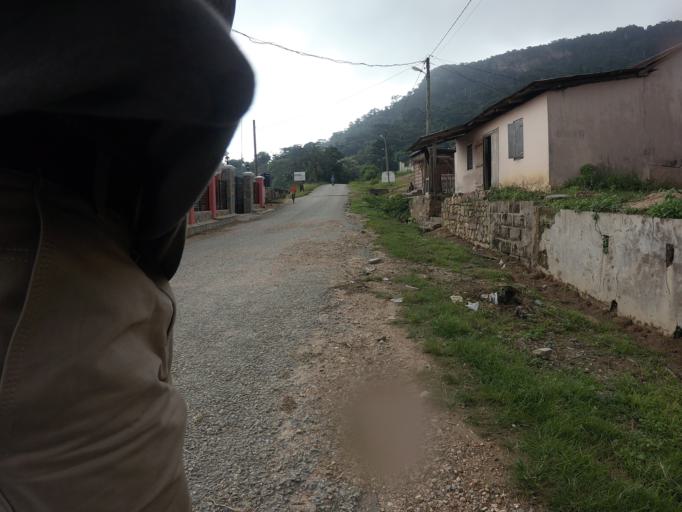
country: GH
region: Volta
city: Kpandu
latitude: 6.8235
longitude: 0.4253
